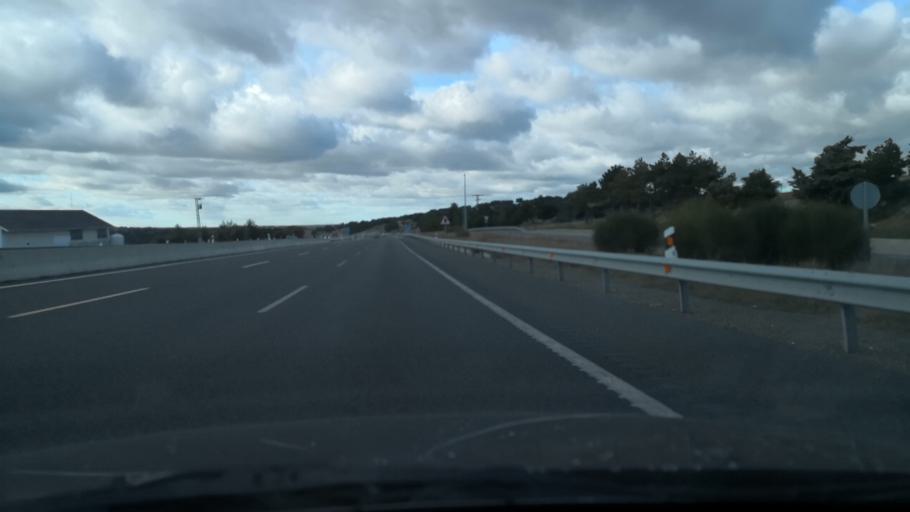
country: ES
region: Castille and Leon
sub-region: Provincia de Segovia
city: Zarzuela del Monte
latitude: 40.7475
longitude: -4.3394
